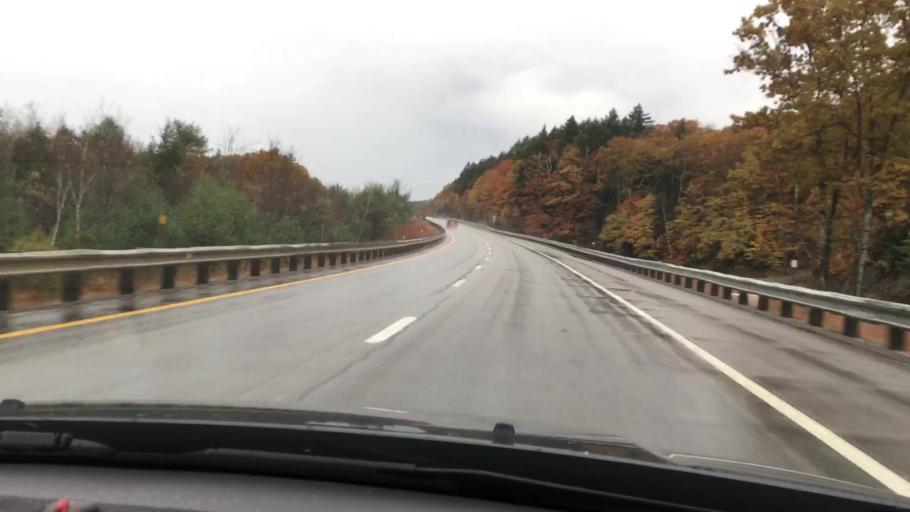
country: US
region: New Hampshire
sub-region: Merrimack County
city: Hill
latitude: 43.5807
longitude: -71.6266
